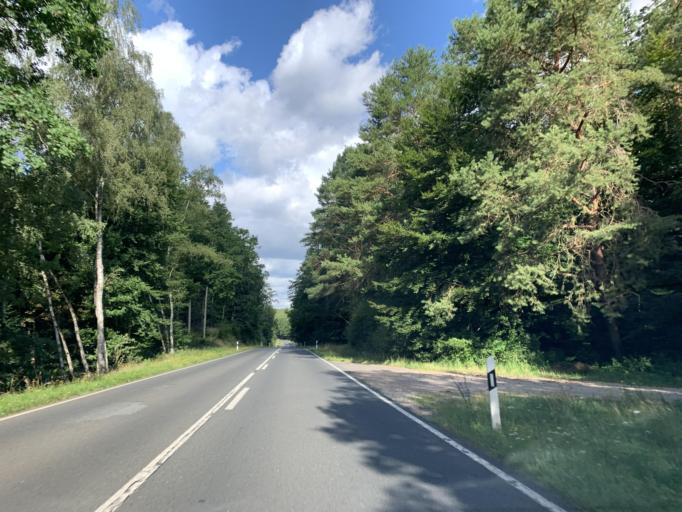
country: DE
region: Mecklenburg-Vorpommern
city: Carpin
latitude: 53.3619
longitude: 13.2166
